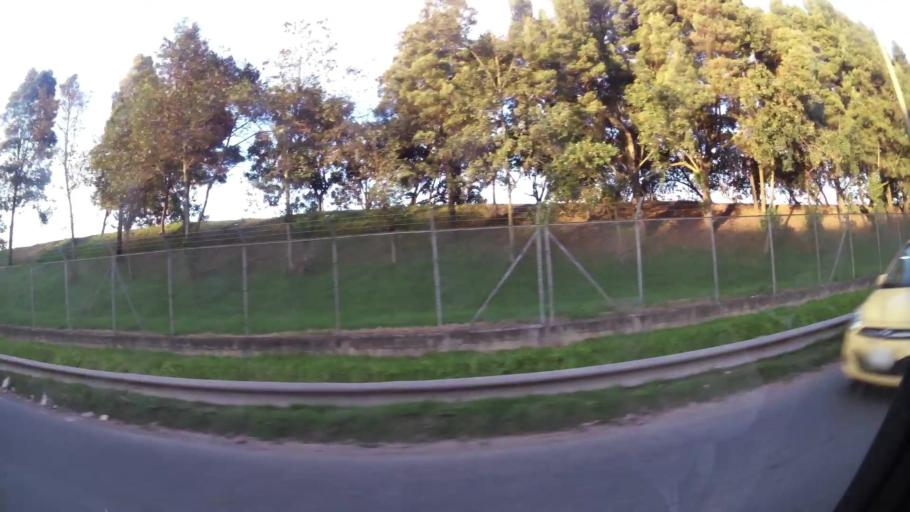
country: CO
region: Cundinamarca
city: Funza
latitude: 4.6923
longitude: -74.1480
